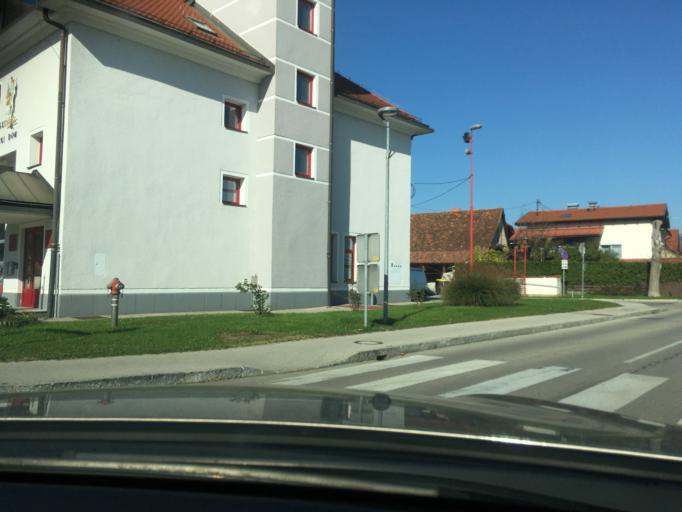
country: SI
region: Menges
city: Menges
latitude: 46.1635
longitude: 14.5720
